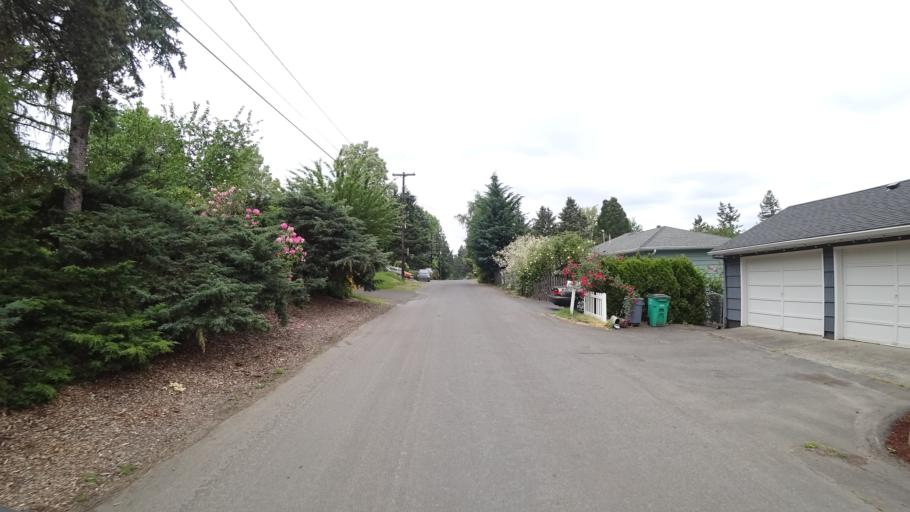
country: US
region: Oregon
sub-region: Washington County
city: Garden Home-Whitford
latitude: 45.4755
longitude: -122.7350
